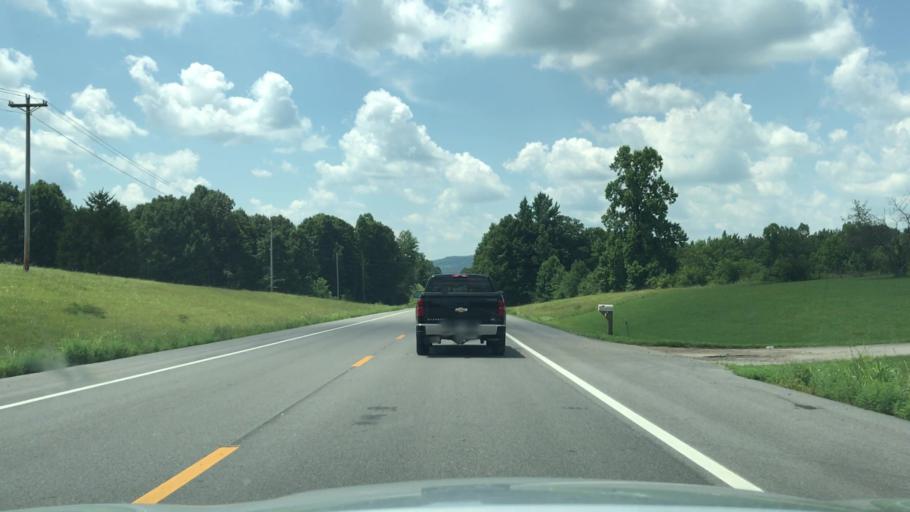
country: US
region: Tennessee
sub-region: Pickett County
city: Byrdstown
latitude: 36.4703
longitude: -85.1959
